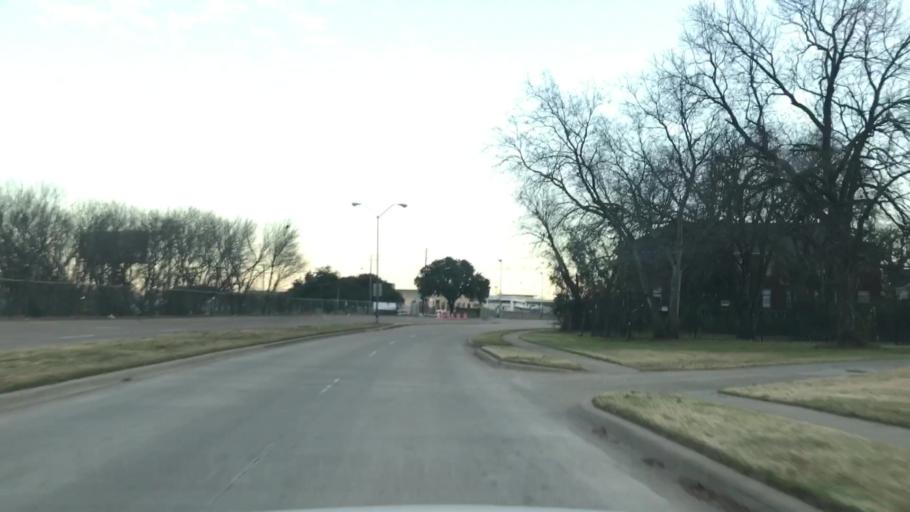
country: US
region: Texas
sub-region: Dallas County
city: Dallas
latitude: 32.7583
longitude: -96.8118
